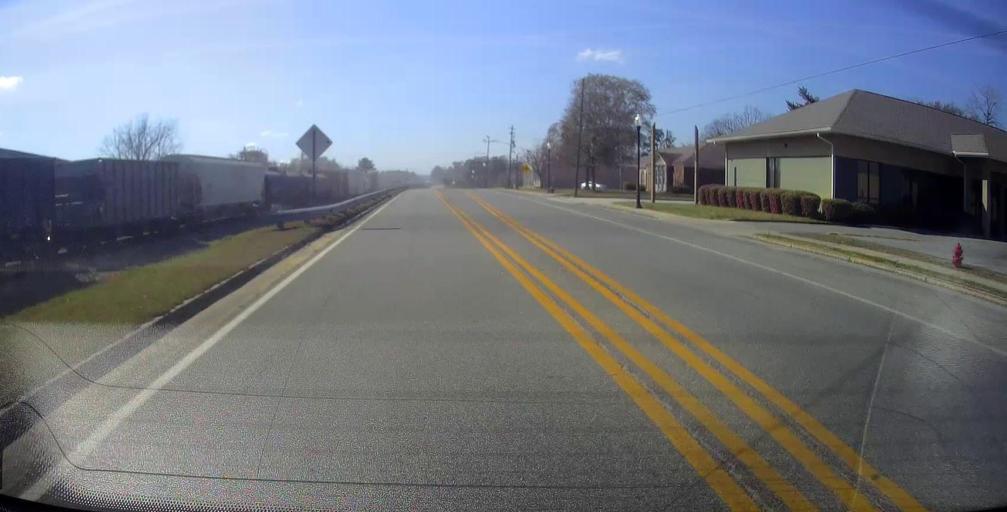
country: US
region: Georgia
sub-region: Wilkinson County
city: Gordon
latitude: 32.8823
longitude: -83.3340
